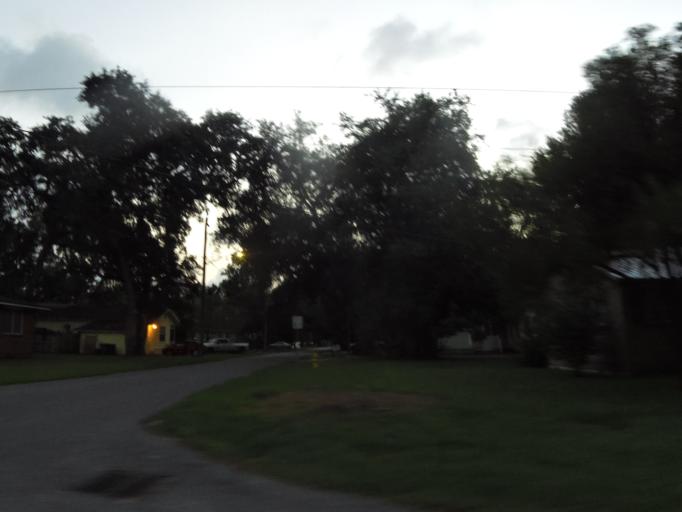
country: US
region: Florida
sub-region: Duval County
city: Jacksonville
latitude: 30.3183
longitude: -81.7139
